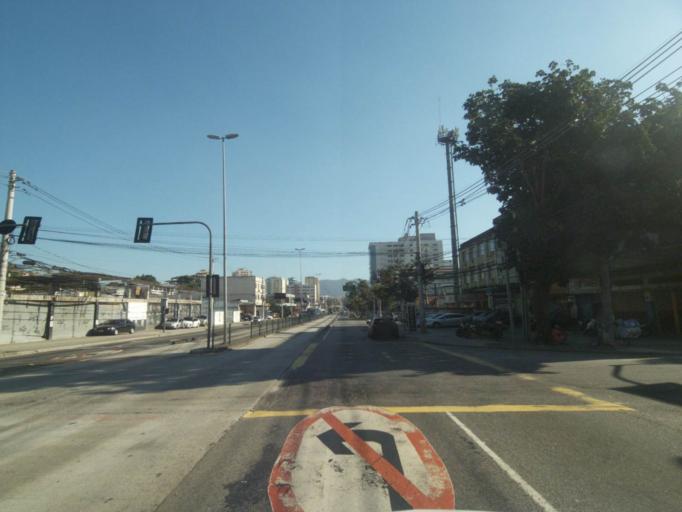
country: BR
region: Rio de Janeiro
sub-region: Sao Joao De Meriti
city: Sao Joao de Meriti
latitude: -22.9185
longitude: -43.3653
